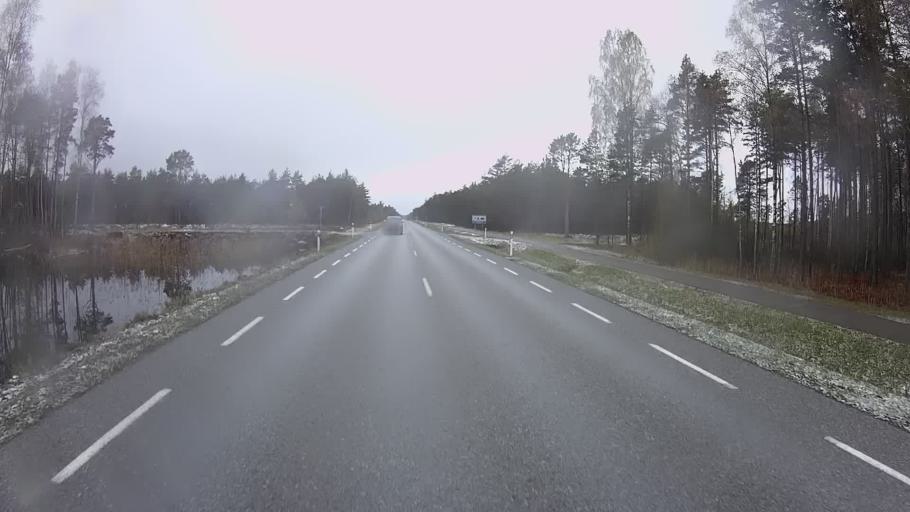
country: EE
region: Hiiumaa
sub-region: Kaerdla linn
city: Kardla
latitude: 59.0093
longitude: 22.6299
